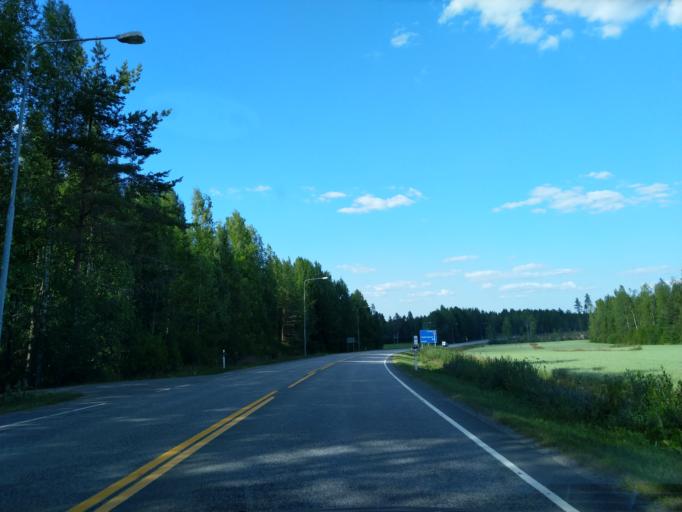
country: FI
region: Pirkanmaa
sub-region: Luoteis-Pirkanmaa
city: Kihnioe
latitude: 62.1948
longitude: 23.1717
